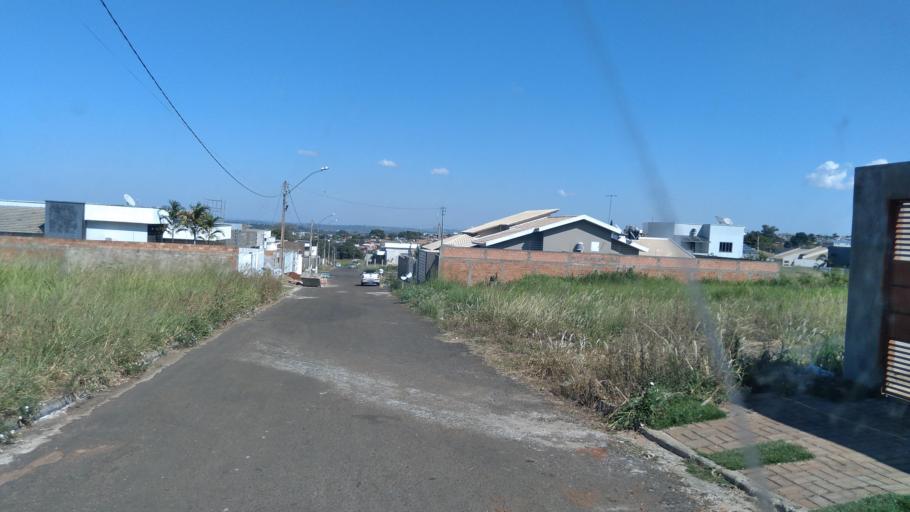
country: BR
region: Goias
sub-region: Mineiros
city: Mineiros
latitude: -17.5514
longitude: -52.5412
